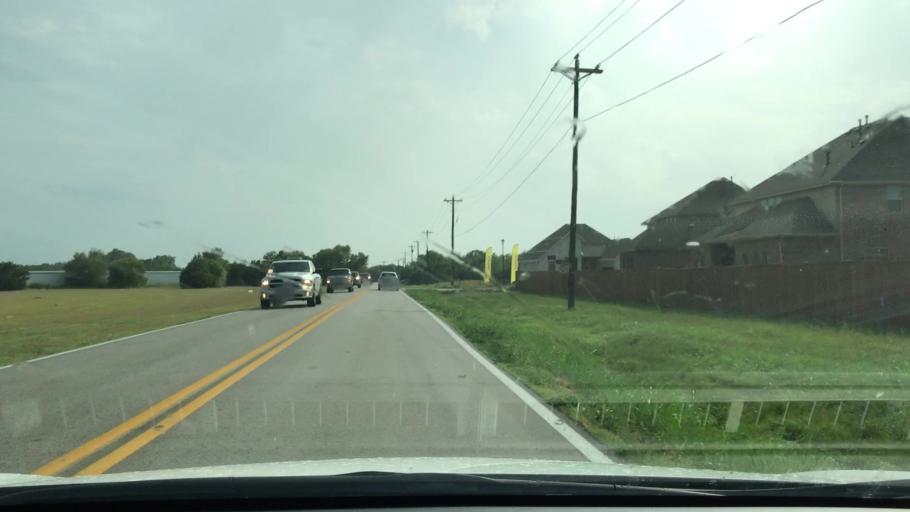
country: US
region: Texas
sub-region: Collin County
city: Wylie
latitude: 32.9821
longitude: -96.5231
